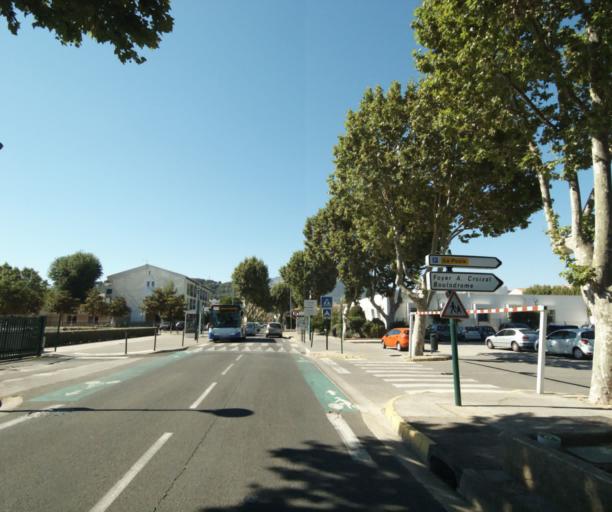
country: FR
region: Provence-Alpes-Cote d'Azur
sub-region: Departement du Var
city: La Garde
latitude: 43.1220
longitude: 6.0101
